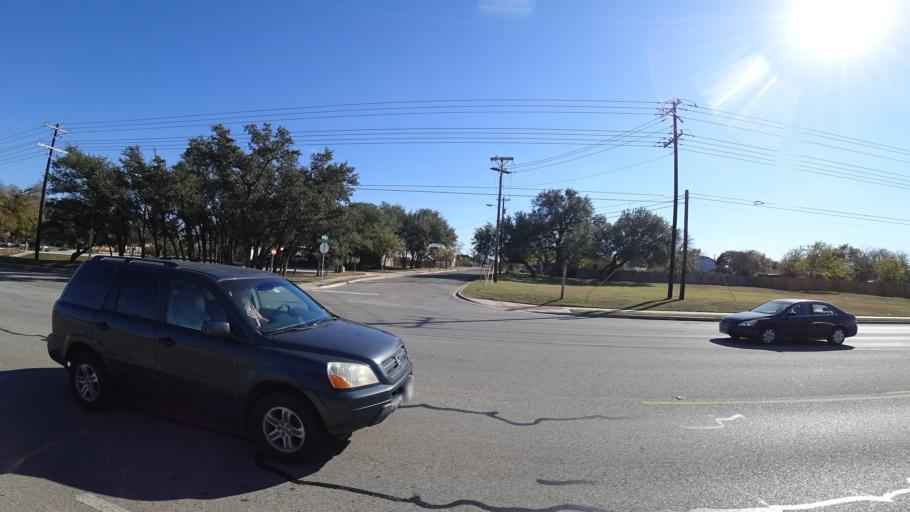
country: US
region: Texas
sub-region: Williamson County
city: Cedar Park
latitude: 30.5316
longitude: -97.8393
